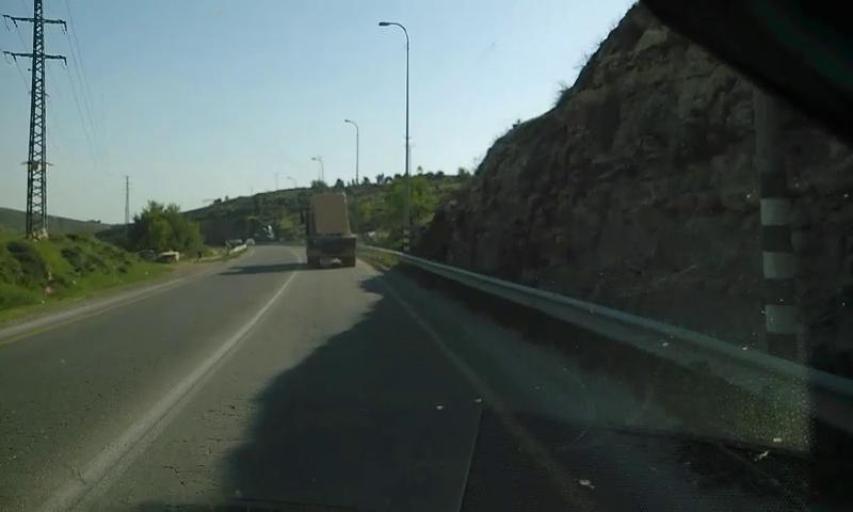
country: PS
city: Khallat ad Dar
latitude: 31.5096
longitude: 35.1321
